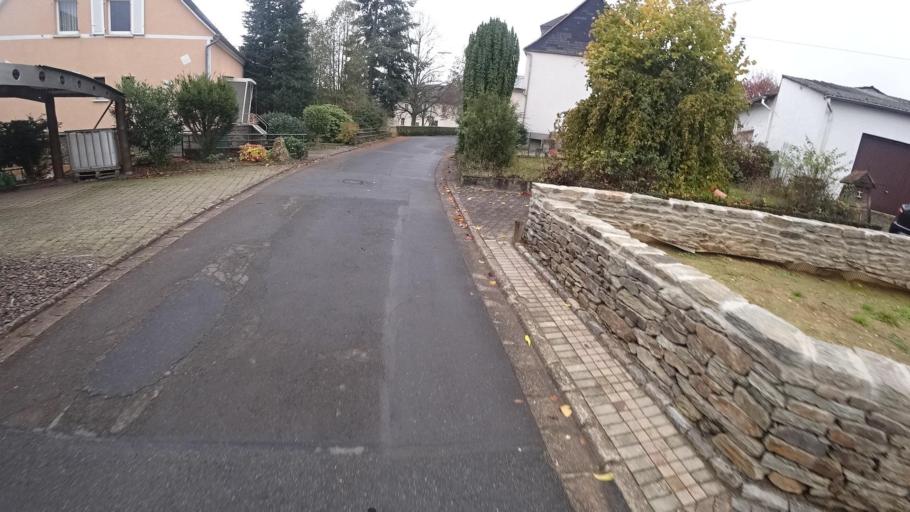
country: DE
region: Rheinland-Pfalz
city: Niederburg
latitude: 50.1192
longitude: 7.6936
